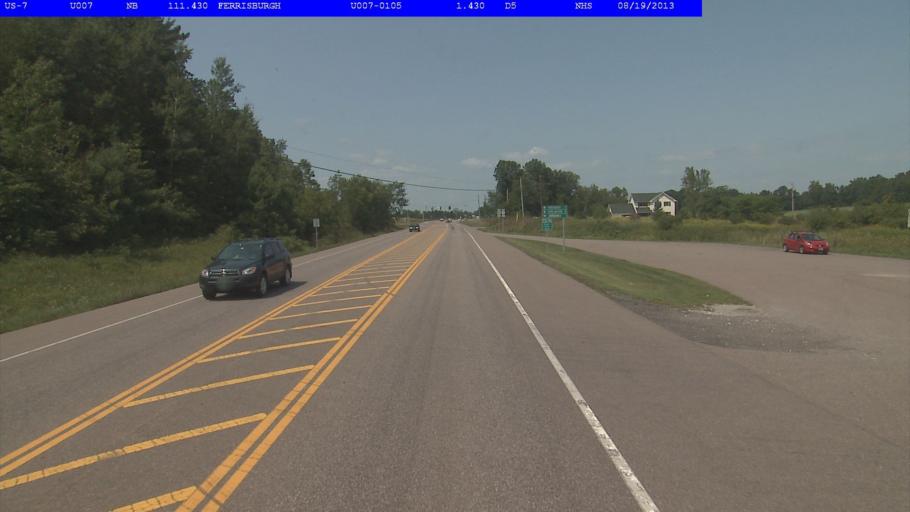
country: US
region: Vermont
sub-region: Addison County
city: Vergennes
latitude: 44.1824
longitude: -73.2395
